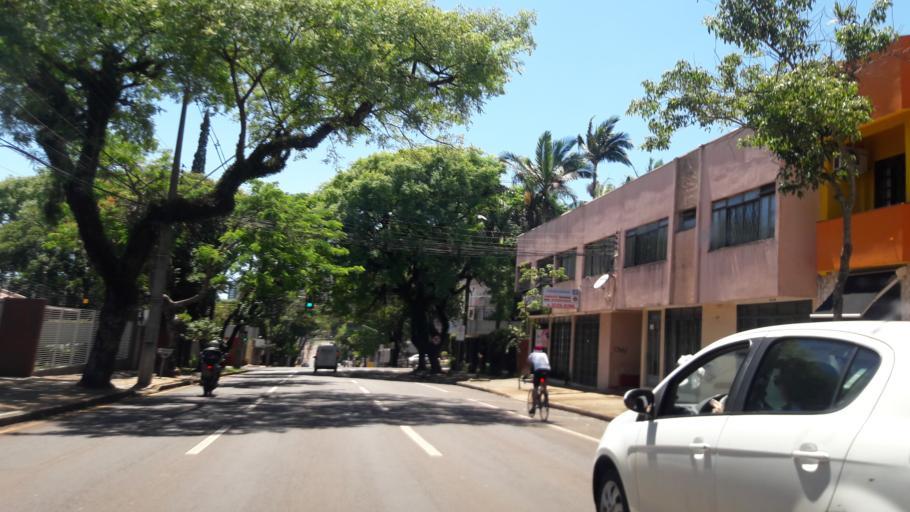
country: BR
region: Parana
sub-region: Cascavel
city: Cascavel
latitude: -24.9520
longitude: -53.4623
